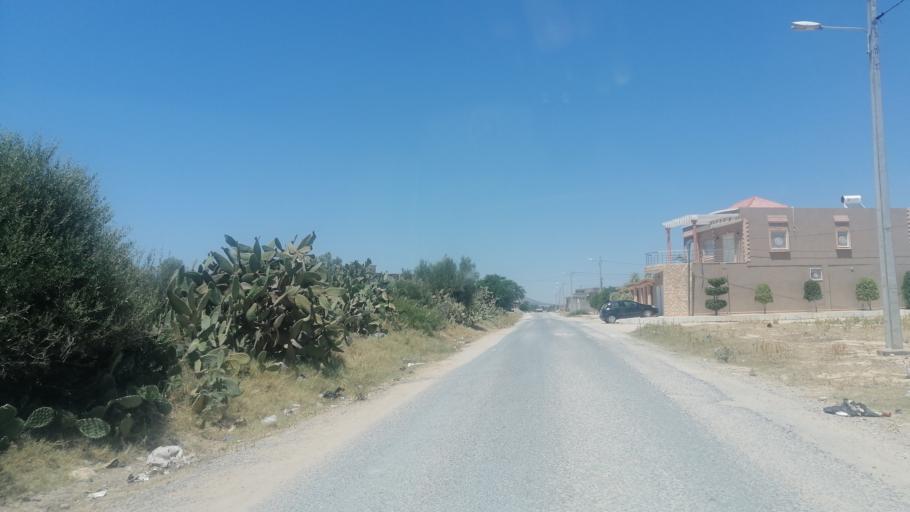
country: TN
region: Al Qayrawan
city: Sbikha
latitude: 36.1231
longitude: 10.0881
